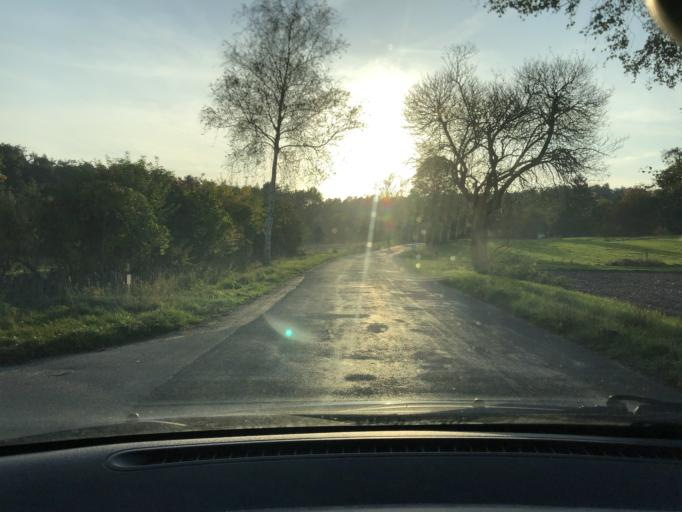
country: DE
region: Lower Saxony
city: Hitzacker
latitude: 53.1270
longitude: 11.0183
